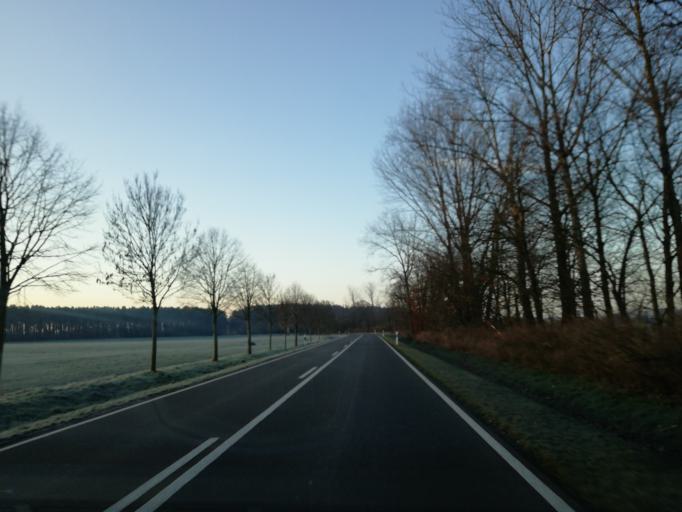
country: DE
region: Brandenburg
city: Crinitz
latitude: 51.6978
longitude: 13.7213
